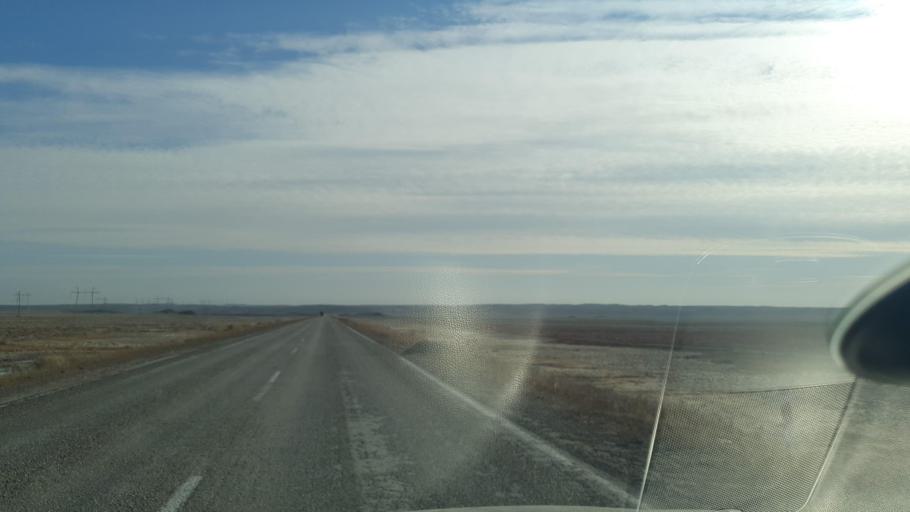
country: KZ
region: Zhambyl
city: Mynaral
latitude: 45.5749
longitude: 73.4141
